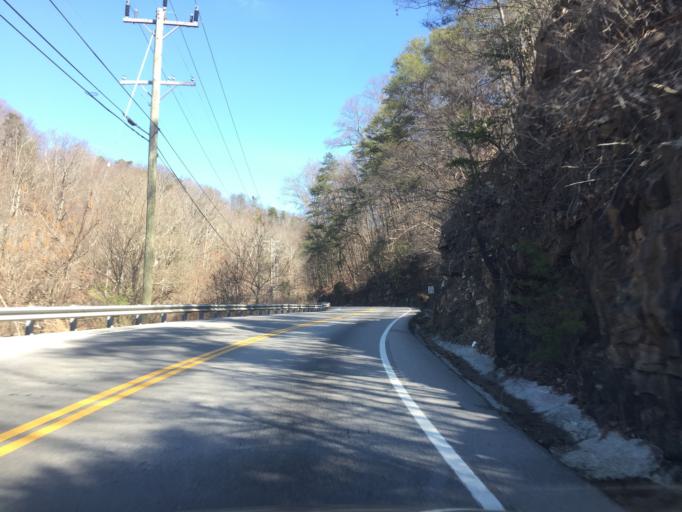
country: US
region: Tennessee
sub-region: Hamilton County
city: Signal Mountain
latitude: 35.1145
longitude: -85.3550
